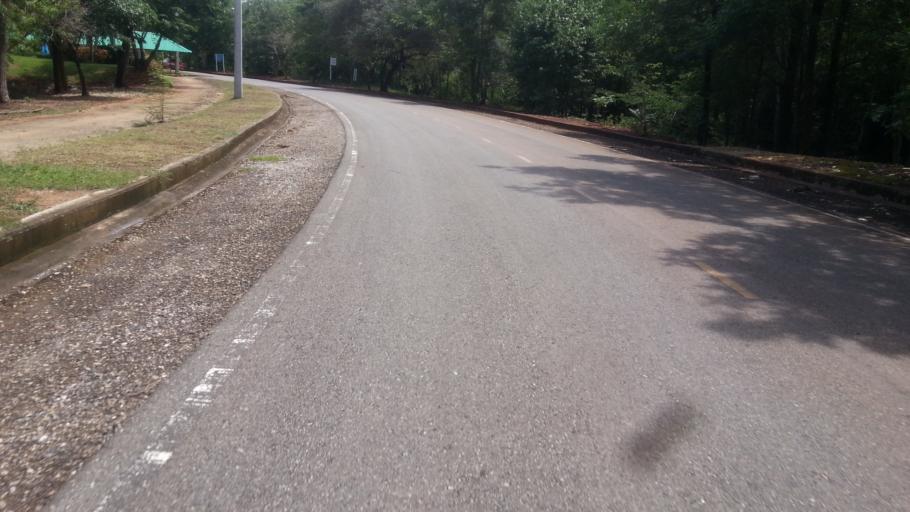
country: TH
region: Kanchanaburi
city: Sai Yok
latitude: 14.1281
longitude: 99.1595
